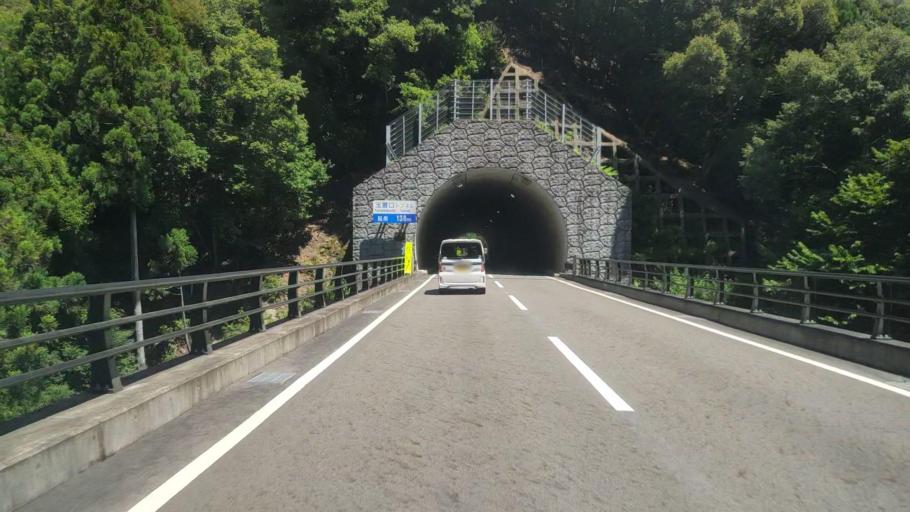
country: JP
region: Wakayama
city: Shingu
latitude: 33.8893
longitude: 135.8798
